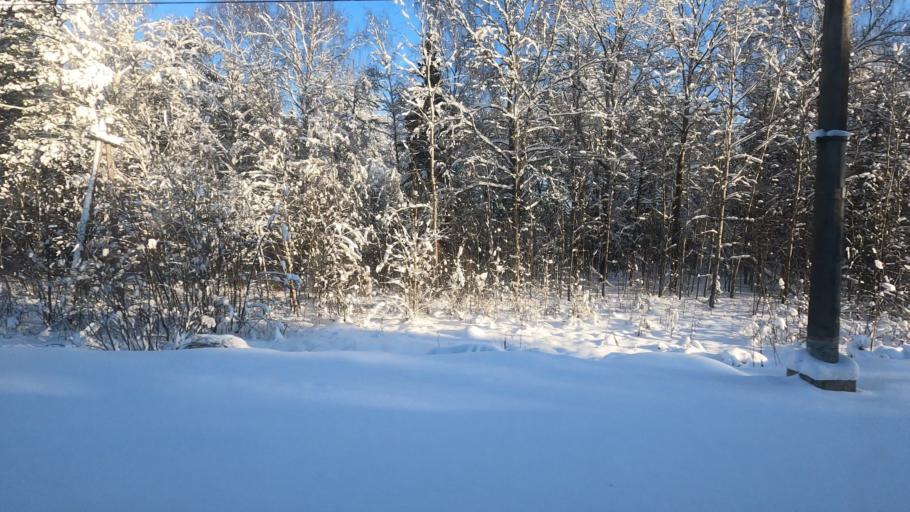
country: RU
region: Moskovskaya
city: Novo-Nikol'skoye
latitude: 56.6370
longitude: 37.5621
